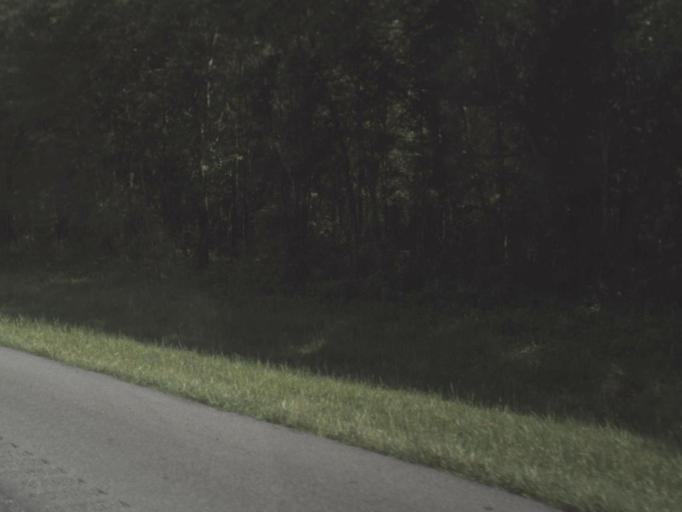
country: US
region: Florida
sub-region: Columbia County
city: Five Points
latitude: 30.2480
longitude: -82.7012
